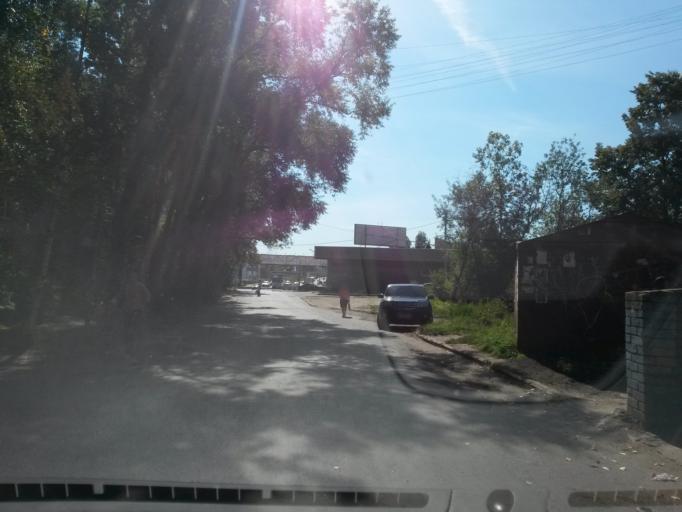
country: RU
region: Jaroslavl
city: Yaroslavl
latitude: 57.5747
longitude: 39.8511
